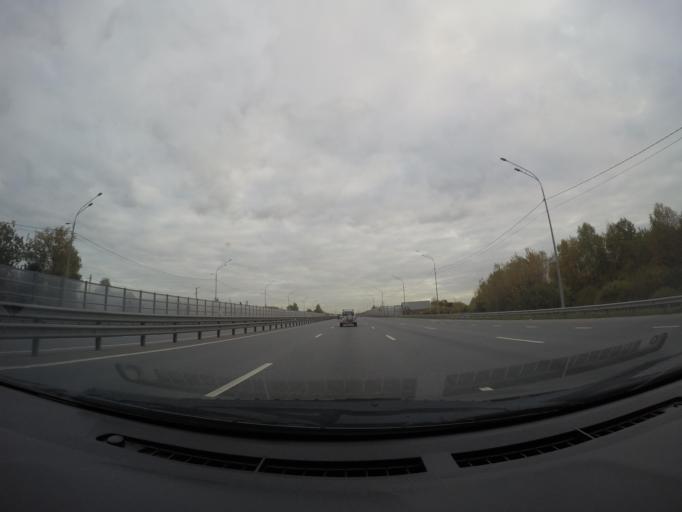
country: RU
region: Moskovskaya
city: Zheleznodorozhnyy
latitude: 55.8035
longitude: 38.0258
